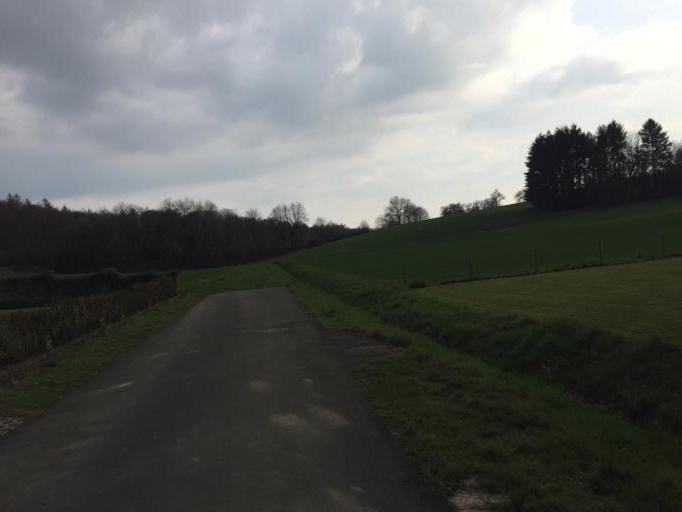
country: DE
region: Hesse
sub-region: Regierungsbezirk Giessen
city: Laubach
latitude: 50.5427
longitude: 8.9535
